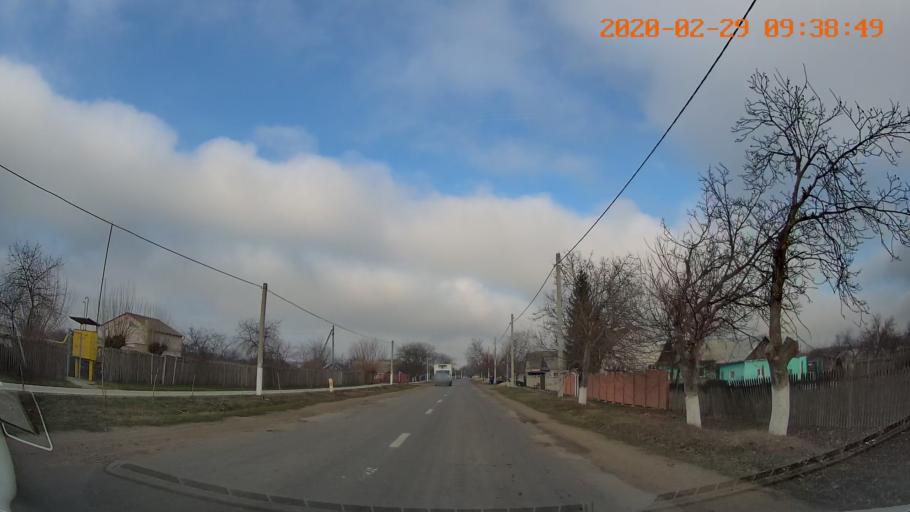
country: MD
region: Telenesti
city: Dnestrovsc
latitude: 46.6326
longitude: 29.8620
